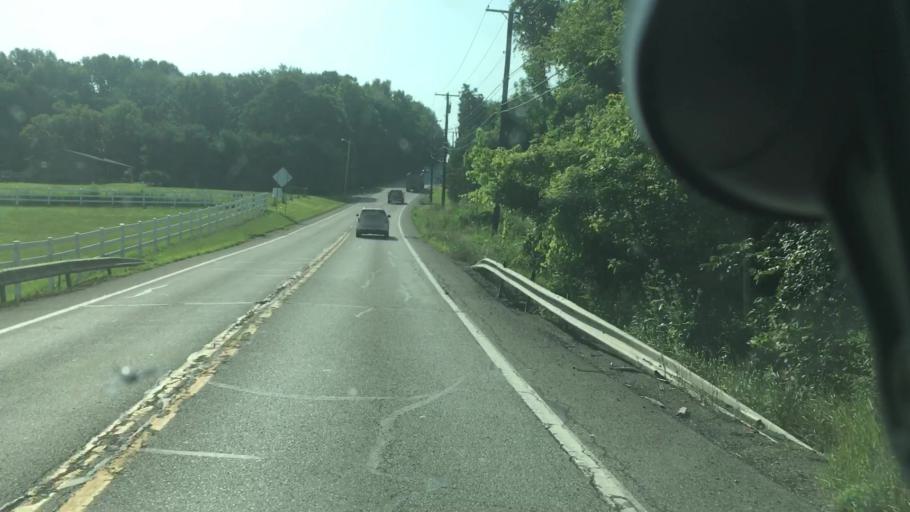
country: US
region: Pennsylvania
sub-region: Lawrence County
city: Oakwood
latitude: 41.0245
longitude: -80.4298
